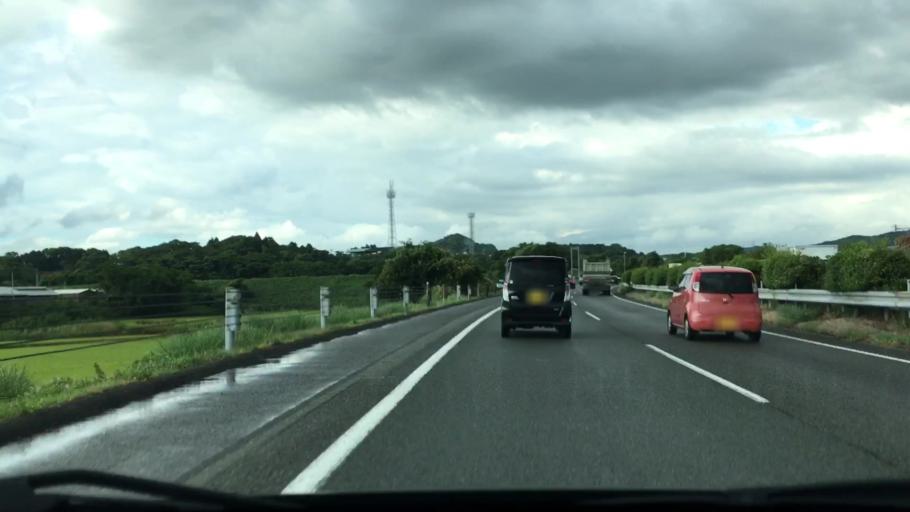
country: JP
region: Fukuoka
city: Koga
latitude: 33.7307
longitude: 130.5064
